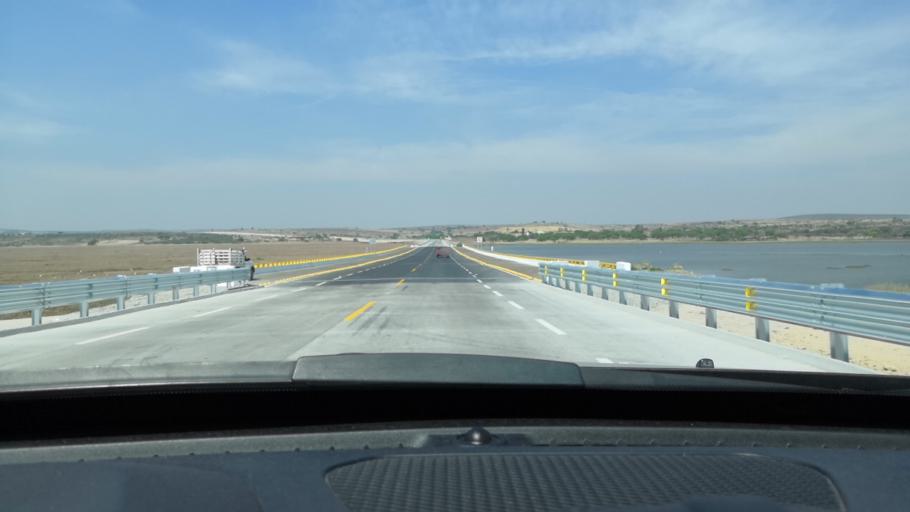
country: MX
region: Guanajuato
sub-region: Purisima del Rincon
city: Potrerillos (Guanajal)
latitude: 21.0840
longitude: -101.8410
